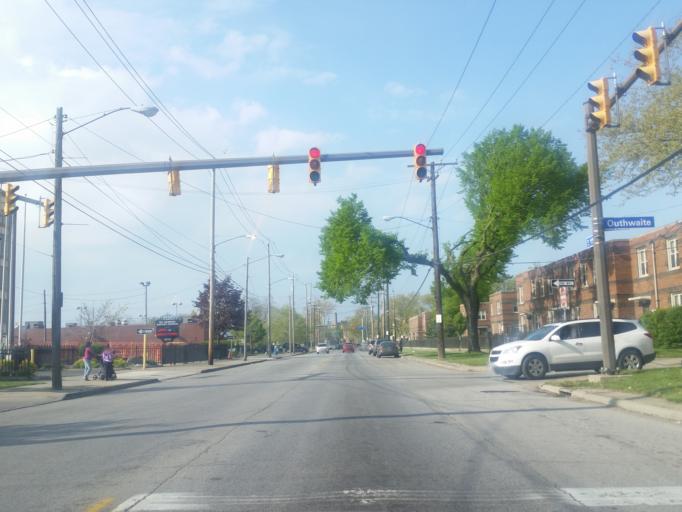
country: US
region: Ohio
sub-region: Cuyahoga County
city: Cleveland
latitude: 41.4909
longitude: -81.6584
